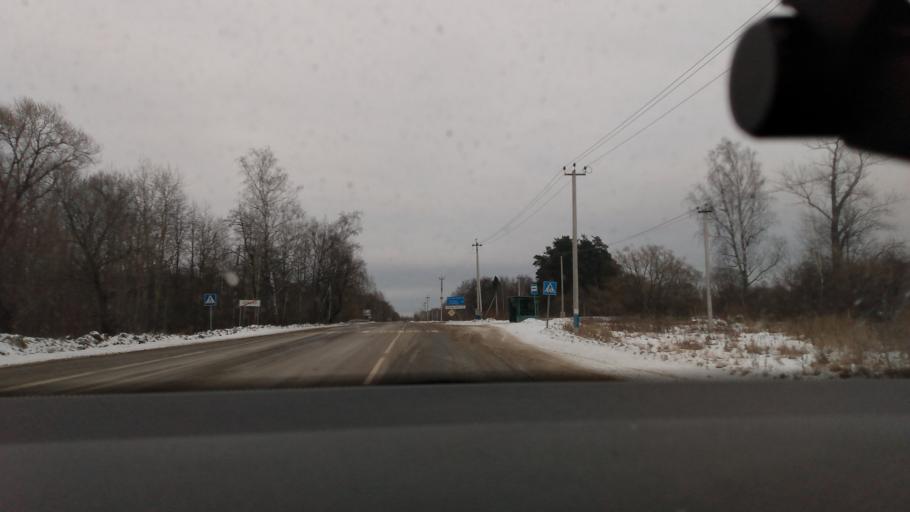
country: RU
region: Moskovskaya
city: Krasnaya Poyma
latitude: 55.1628
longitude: 39.2204
